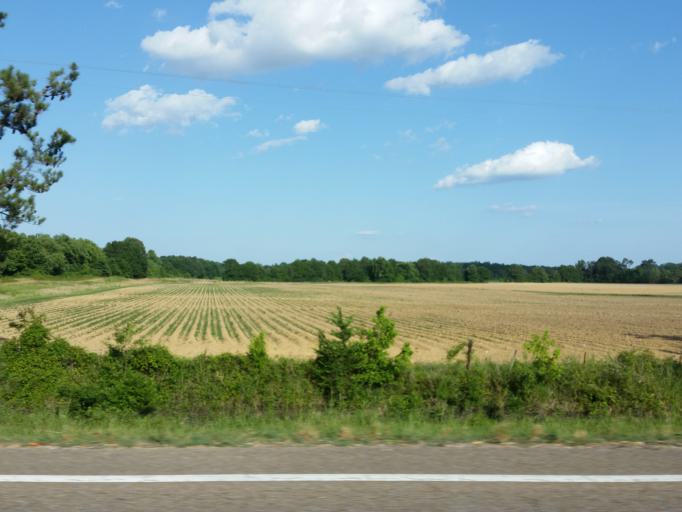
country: US
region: Mississippi
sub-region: Calhoun County
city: Calhoun City
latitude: 33.8141
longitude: -89.3462
